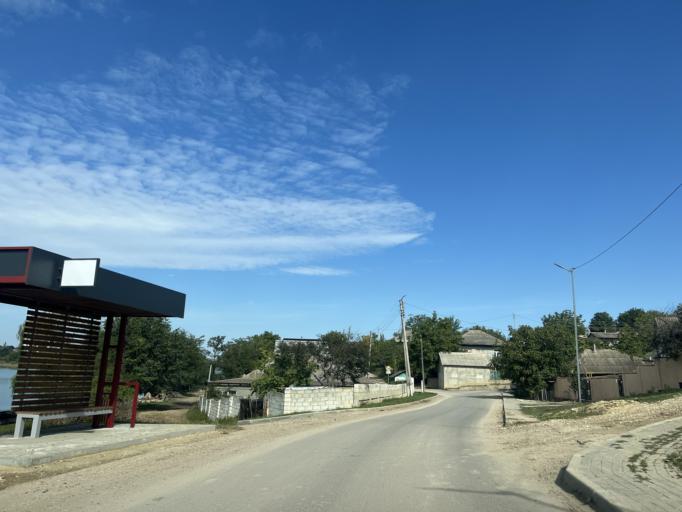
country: MD
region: Ungheni
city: Ungheni
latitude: 47.2004
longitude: 27.8097
